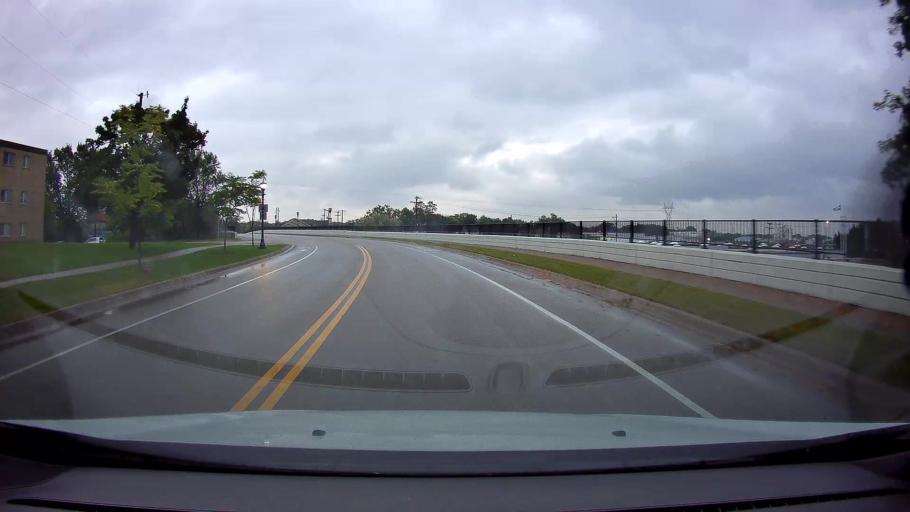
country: US
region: Minnesota
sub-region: Ramsey County
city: Lauderdale
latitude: 44.9715
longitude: -93.1965
